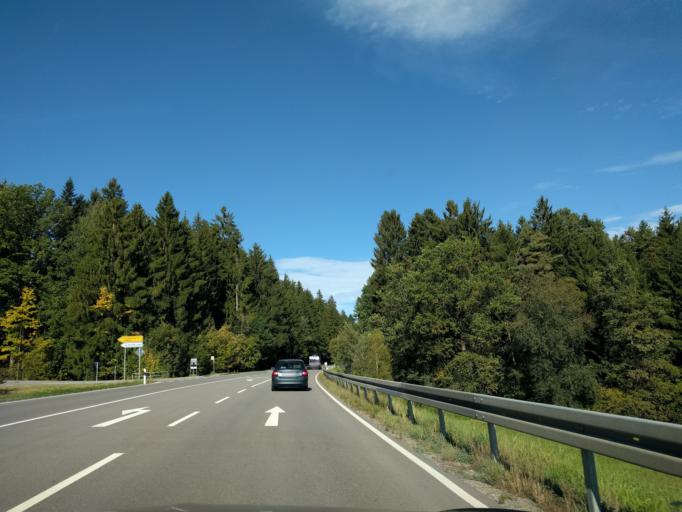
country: DE
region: Bavaria
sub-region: Lower Bavaria
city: Patersdorf
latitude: 49.0278
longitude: 12.9677
